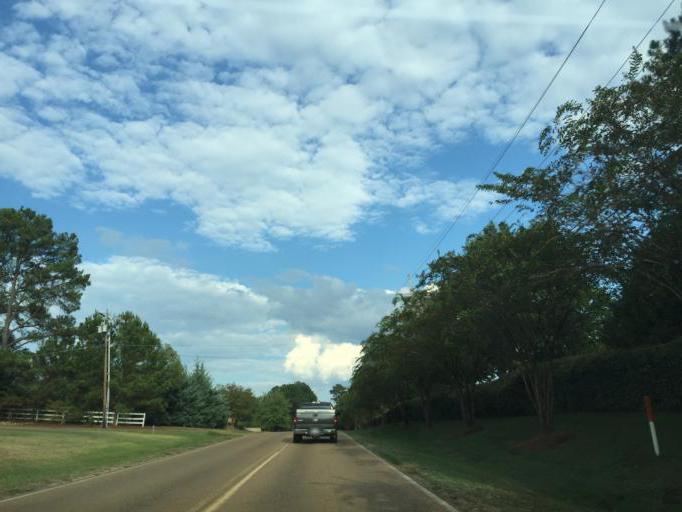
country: US
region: Mississippi
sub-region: Madison County
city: Madison
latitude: 32.4650
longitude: -90.0780
